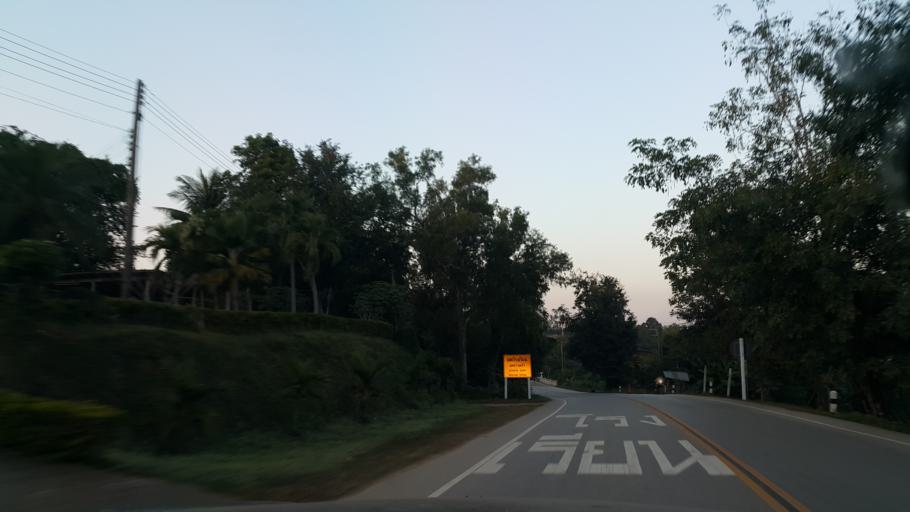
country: TH
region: Phrae
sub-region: Amphoe Wang Chin
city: Wang Chin
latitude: 17.8755
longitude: 99.6194
